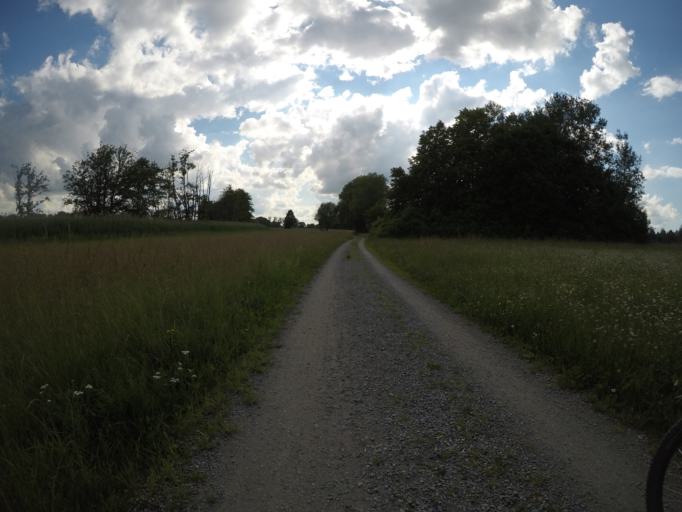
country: DE
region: Bavaria
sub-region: Lower Bavaria
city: Marklkofen
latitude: 48.5650
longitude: 12.5655
